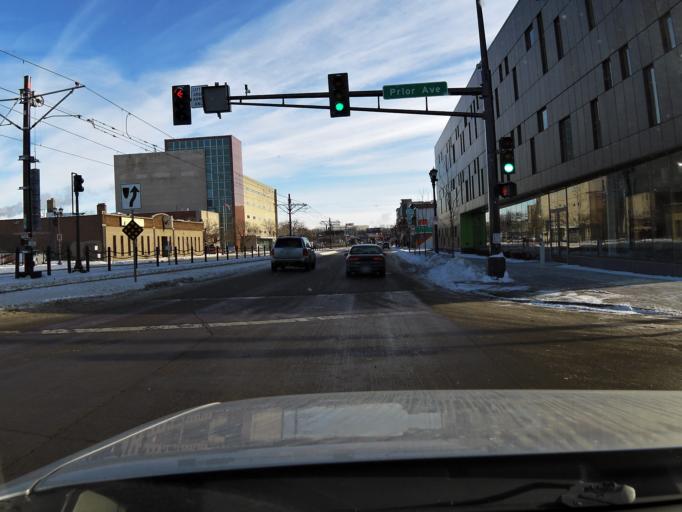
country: US
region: Minnesota
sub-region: Ramsey County
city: Falcon Heights
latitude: 44.9576
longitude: -93.1822
